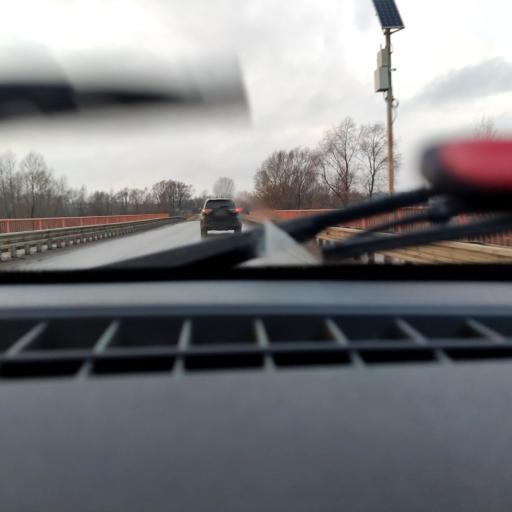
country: RU
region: Bashkortostan
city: Avdon
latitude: 54.5012
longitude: 55.8807
